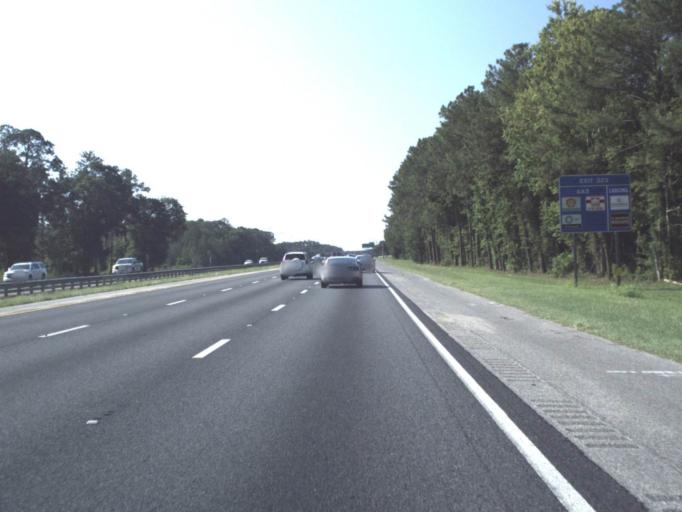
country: US
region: Florida
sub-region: Saint Johns County
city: Villano Beach
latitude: 29.9969
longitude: -81.4685
